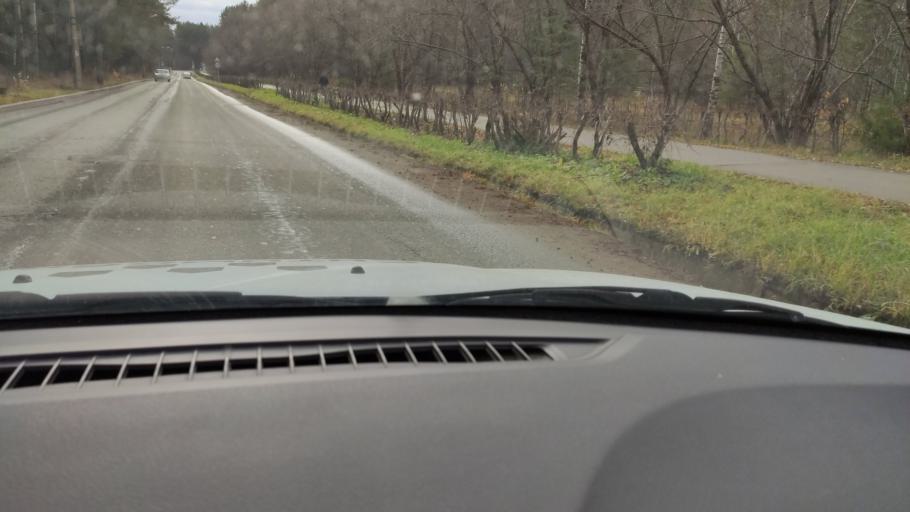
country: RU
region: Perm
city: Perm
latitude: 58.0517
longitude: 56.2140
